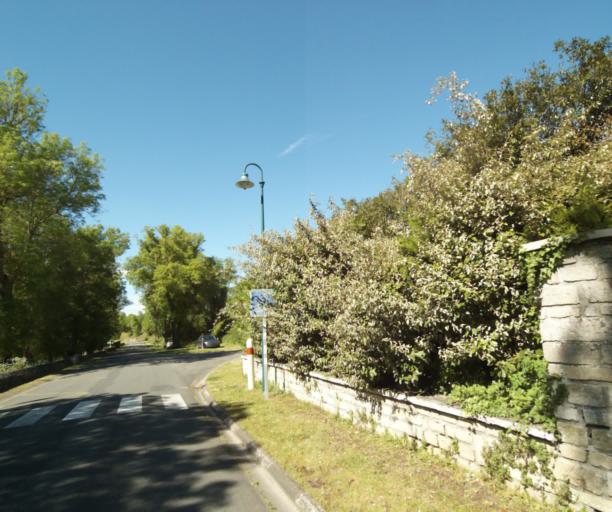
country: FR
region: Poitou-Charentes
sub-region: Departement de la Charente-Maritime
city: Bussac-sur-Charente
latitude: 45.8213
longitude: -0.6387
